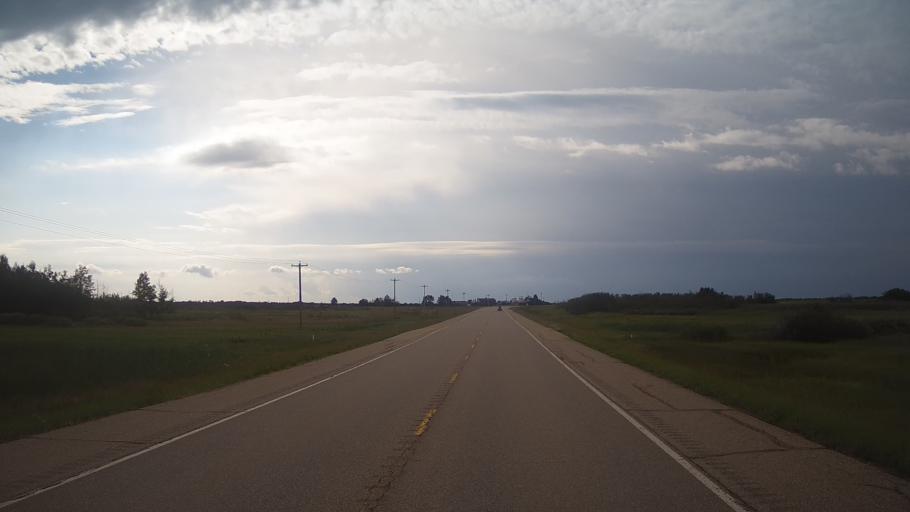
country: CA
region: Alberta
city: Viking
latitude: 53.1343
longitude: -111.9197
